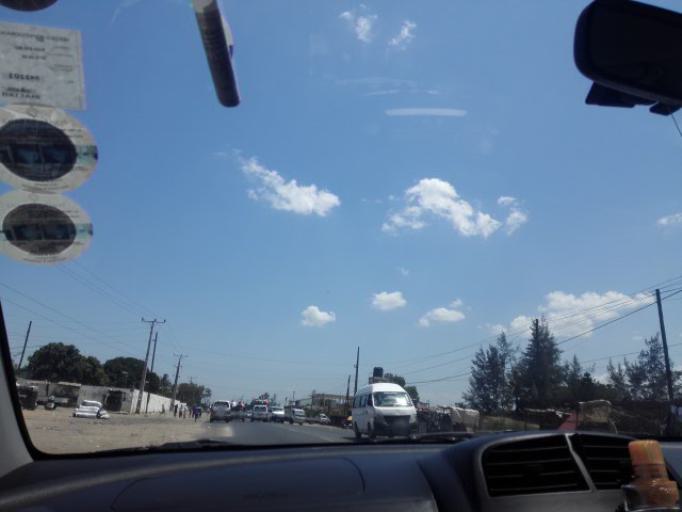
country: MZ
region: Maputo City
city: Maputo
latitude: -25.8547
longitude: 32.5674
